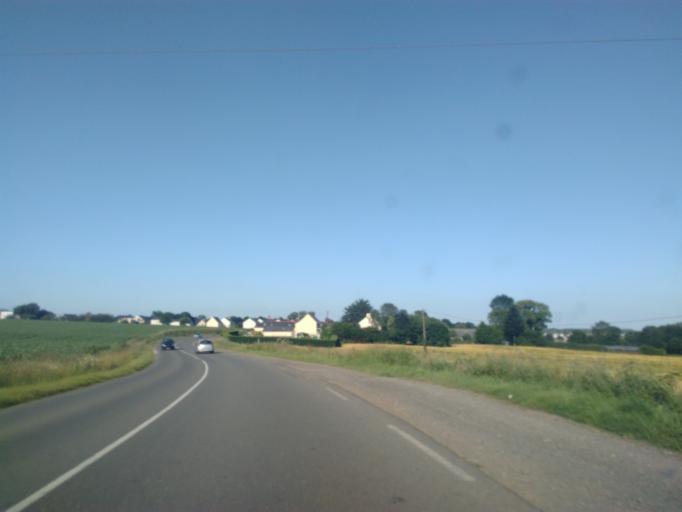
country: FR
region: Brittany
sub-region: Departement d'Ille-et-Vilaine
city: Geveze
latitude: 48.2204
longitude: -1.8078
